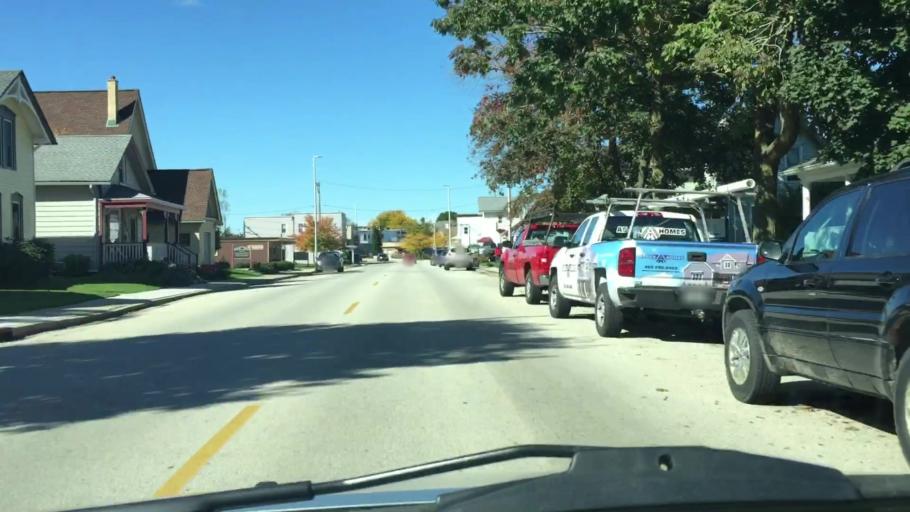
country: US
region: Wisconsin
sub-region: Waukesha County
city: Pewaukee
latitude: 43.0831
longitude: -88.2589
